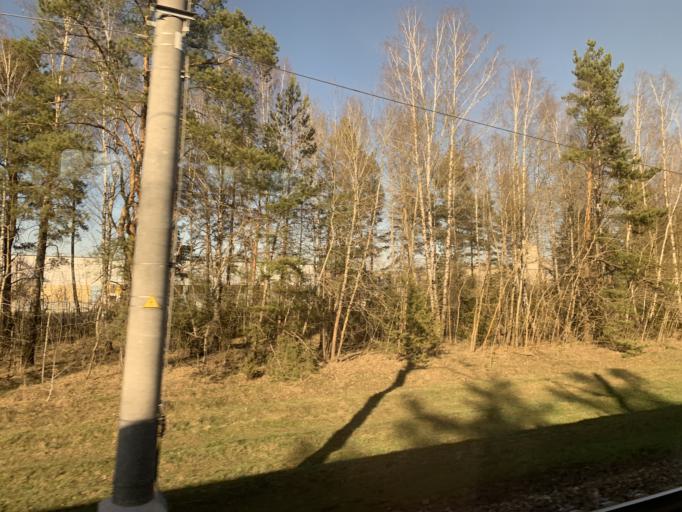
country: BY
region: Grodnenskaya
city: Smarhon'
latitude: 54.4386
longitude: 26.5087
